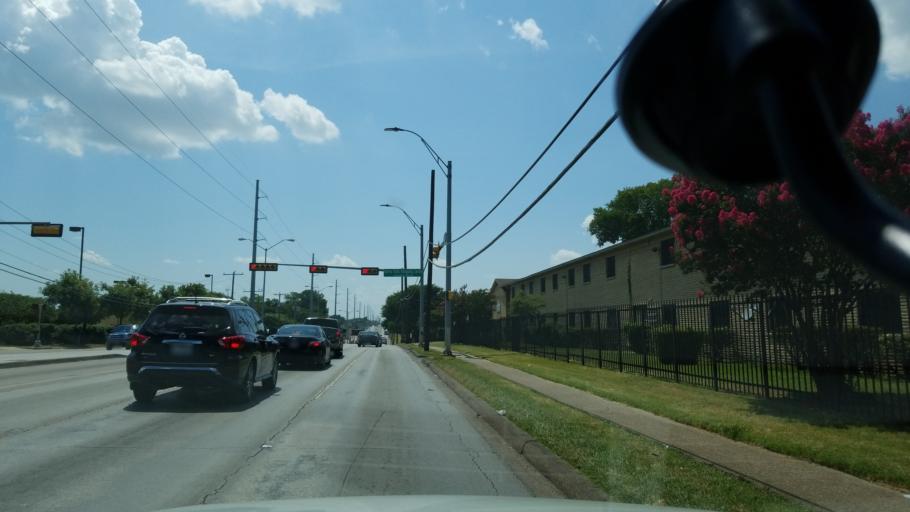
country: US
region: Texas
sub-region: Dallas County
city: Cockrell Hill
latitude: 32.7204
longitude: -96.8760
